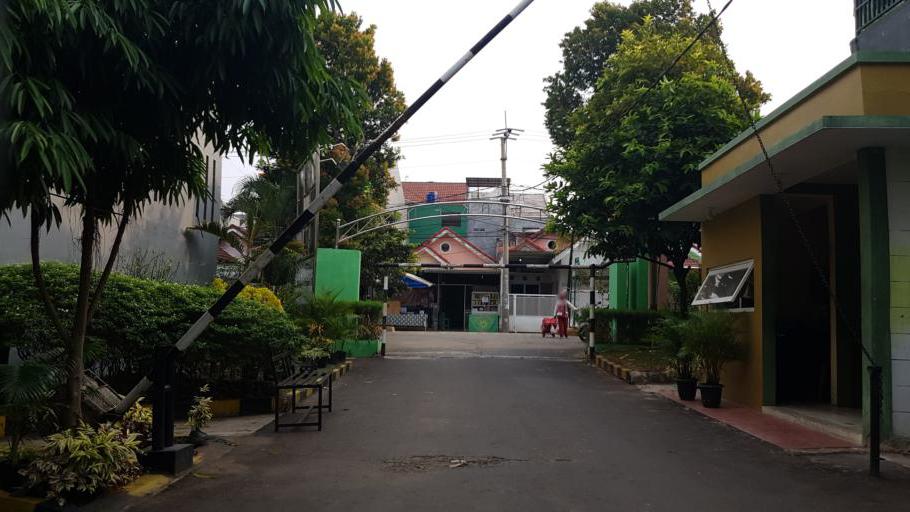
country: ID
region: West Java
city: Sawangan
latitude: -6.3721
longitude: 106.7942
